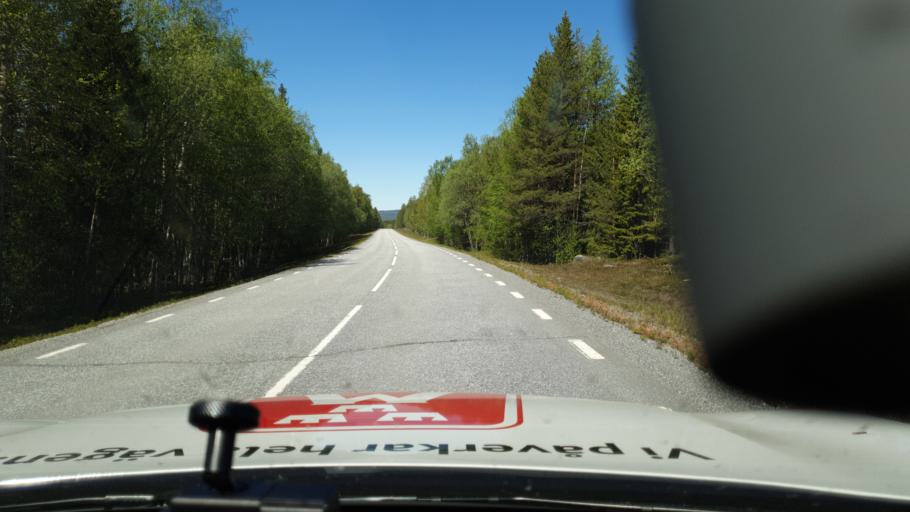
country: SE
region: Vaesterbotten
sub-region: Storumans Kommun
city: Storuman
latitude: 65.1907
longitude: 17.0193
